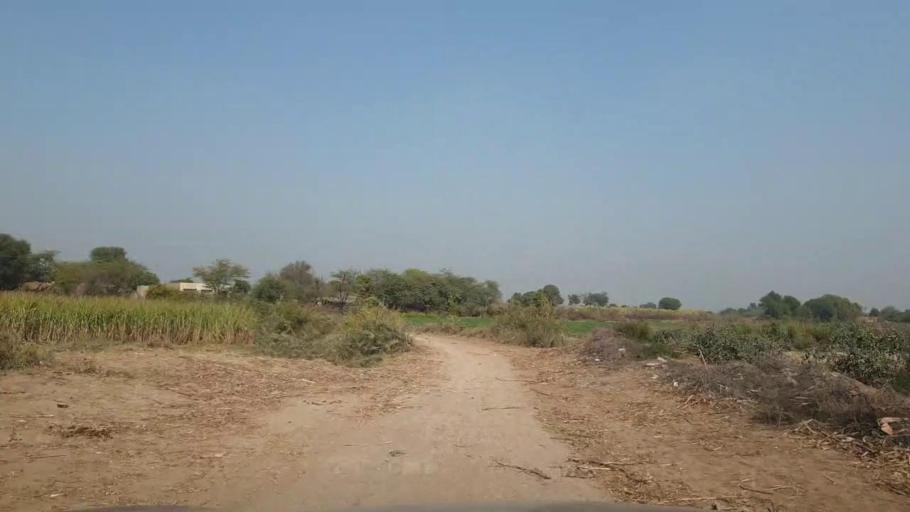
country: PK
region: Sindh
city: Tando Allahyar
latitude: 25.5523
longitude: 68.7242
